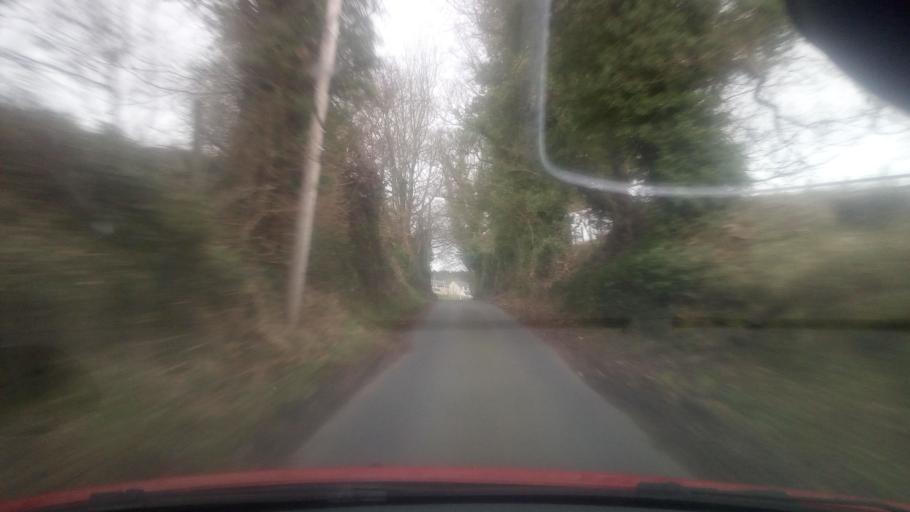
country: GB
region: Scotland
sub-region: The Scottish Borders
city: Jedburgh
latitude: 55.4763
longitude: -2.5427
